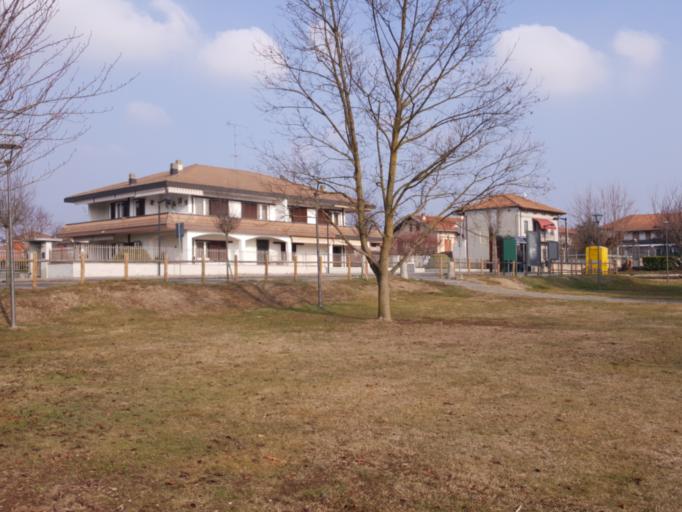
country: IT
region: Piedmont
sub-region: Provincia di Novara
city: Cressa
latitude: 45.6462
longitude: 8.5057
